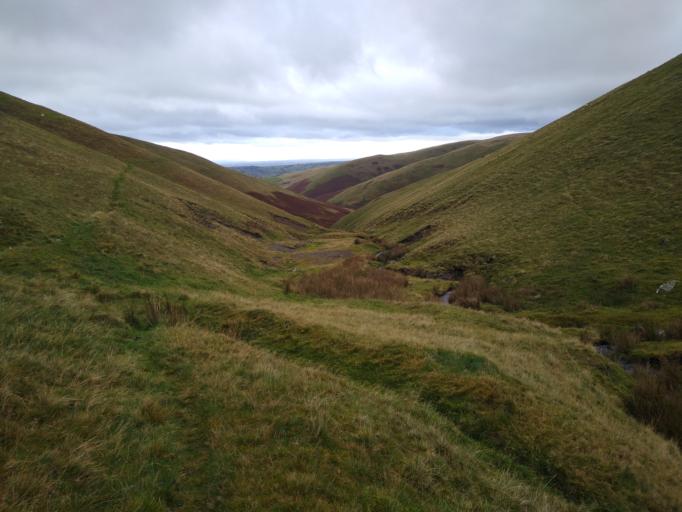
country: GB
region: England
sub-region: Cumbria
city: Keswick
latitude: 54.7034
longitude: -3.0952
